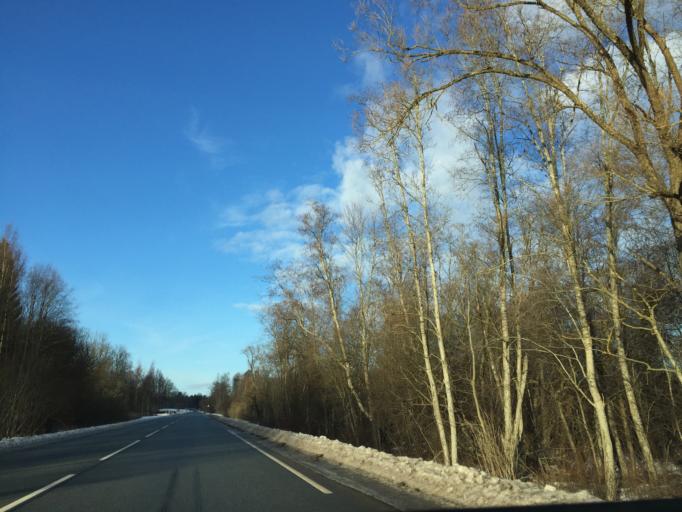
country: LV
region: Ogre
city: Jumprava
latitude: 56.6451
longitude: 24.8837
